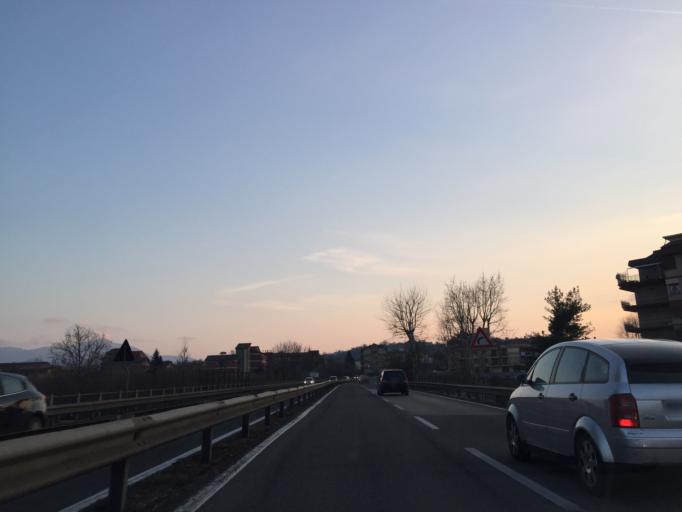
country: IT
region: Campania
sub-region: Provincia di Avellino
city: Atripalda
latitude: 40.9180
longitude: 14.8260
